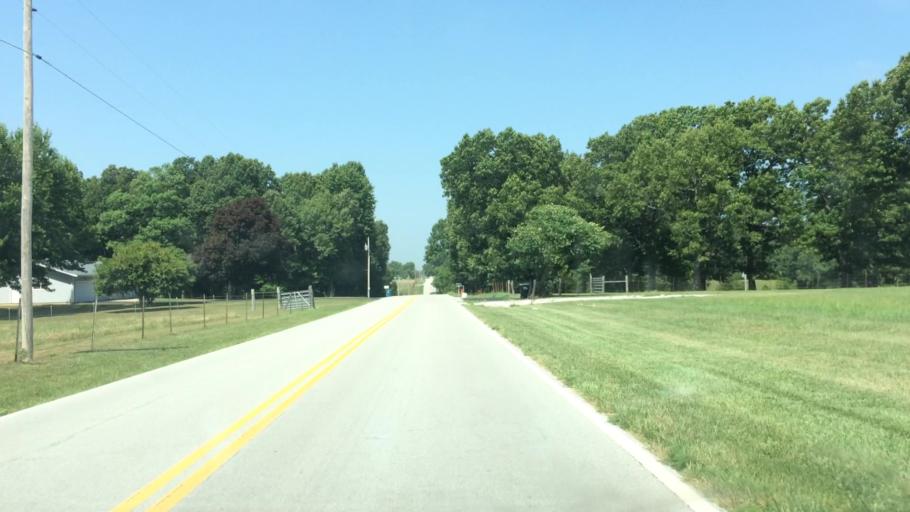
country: US
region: Missouri
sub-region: Greene County
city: Strafford
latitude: 37.2722
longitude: -93.1997
